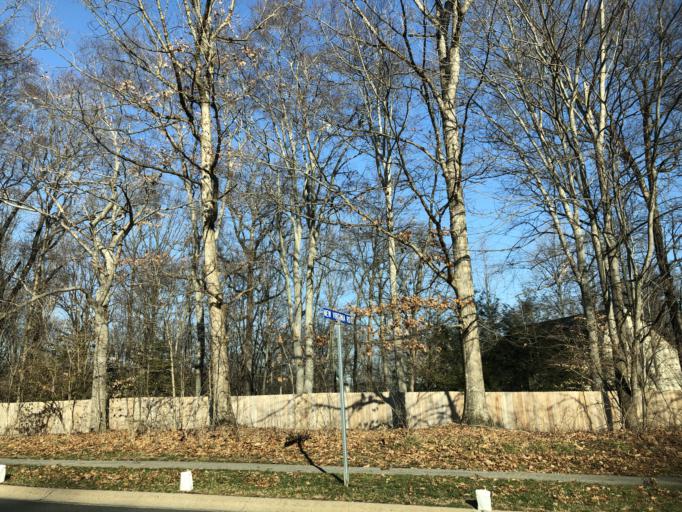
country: US
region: Pennsylvania
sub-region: Chester County
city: Downingtown
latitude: 39.9897
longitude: -75.7030
